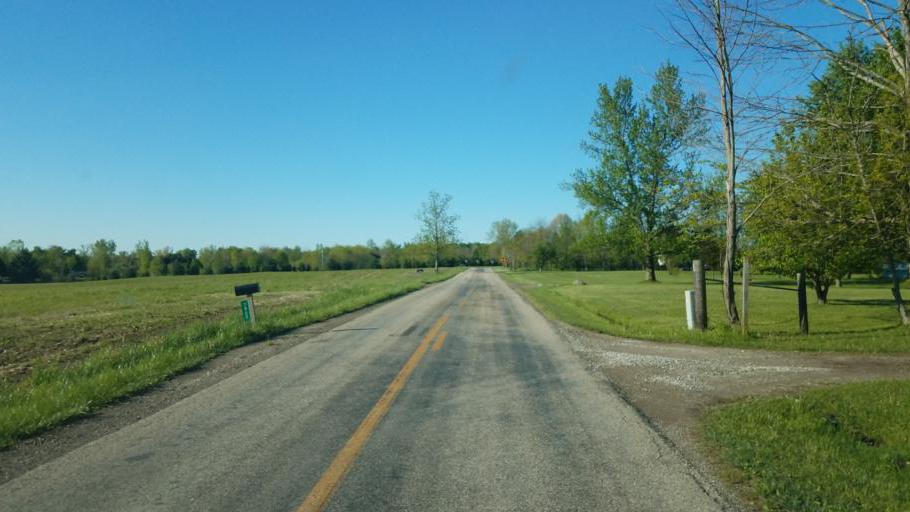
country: US
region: Ohio
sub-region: Delaware County
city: Sunbury
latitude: 40.3412
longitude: -82.8245
